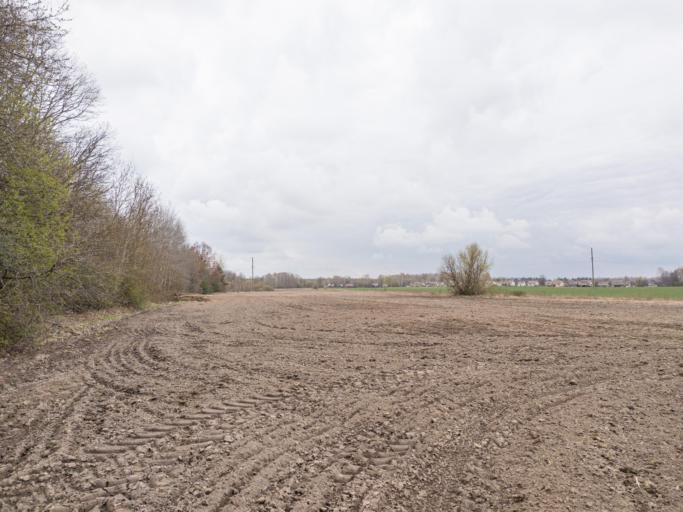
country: BY
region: Brest
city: Pruzhany
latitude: 52.4897
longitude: 24.6315
